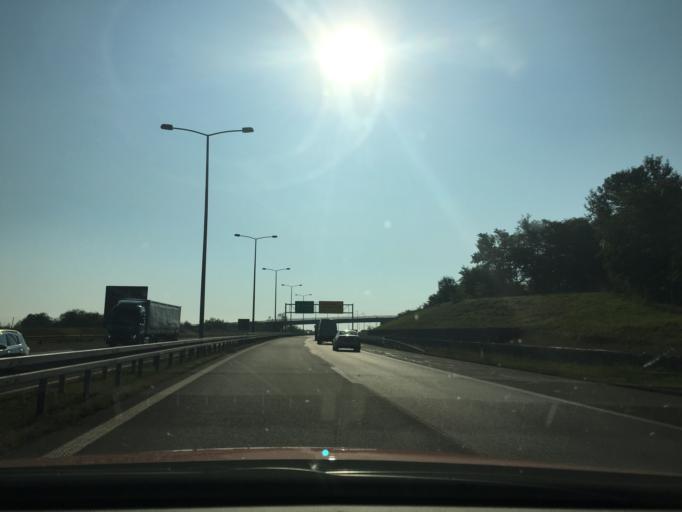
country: RS
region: Central Serbia
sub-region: Podunavski Okrug
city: Smederevo
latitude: 44.5832
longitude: 20.9719
